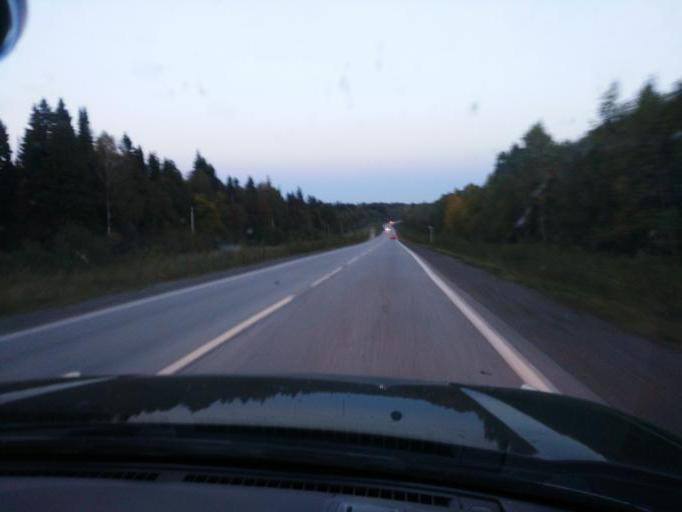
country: RU
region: Perm
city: Verkhnechusovskiye Gorodki
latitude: 58.2590
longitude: 56.9876
